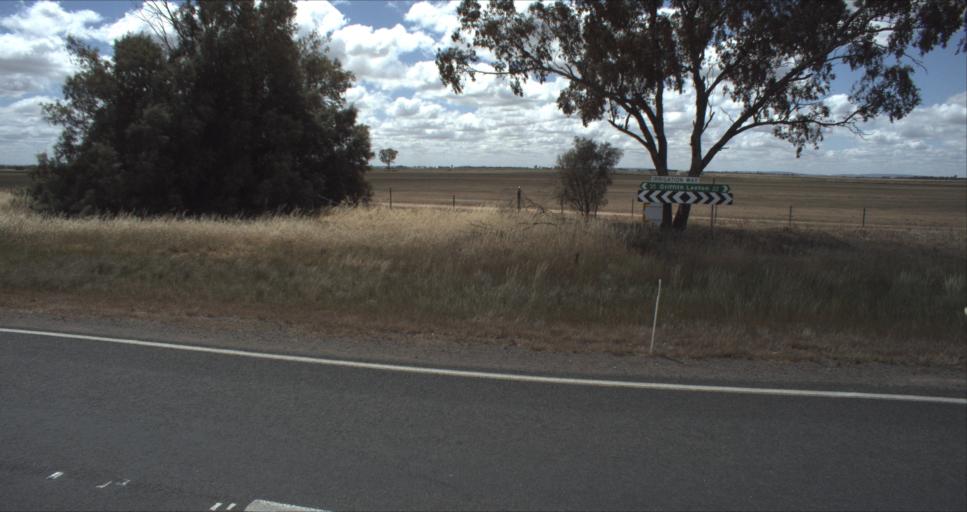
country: AU
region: New South Wales
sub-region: Murrumbidgee Shire
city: Darlington Point
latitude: -34.5030
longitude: 146.1885
